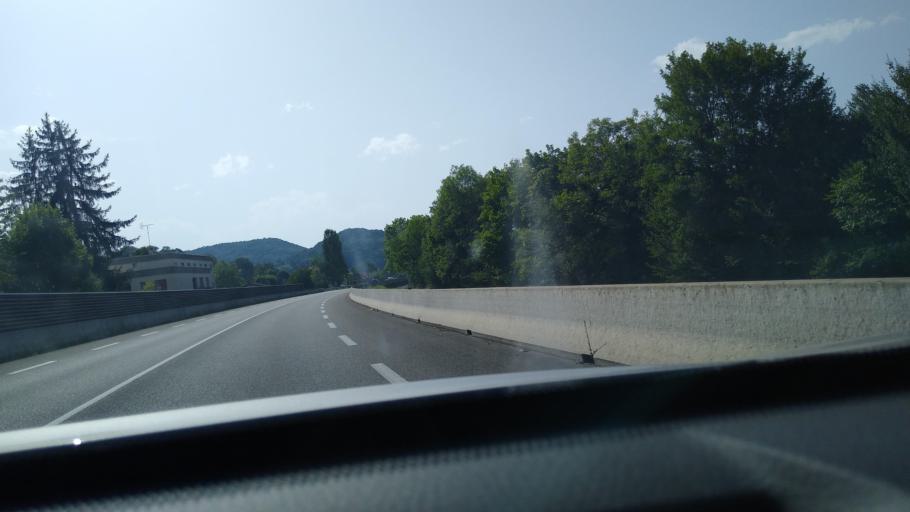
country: FR
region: Midi-Pyrenees
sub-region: Departement de la Haute-Garonne
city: Salies-du-Salat
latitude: 43.0319
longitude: 1.0152
